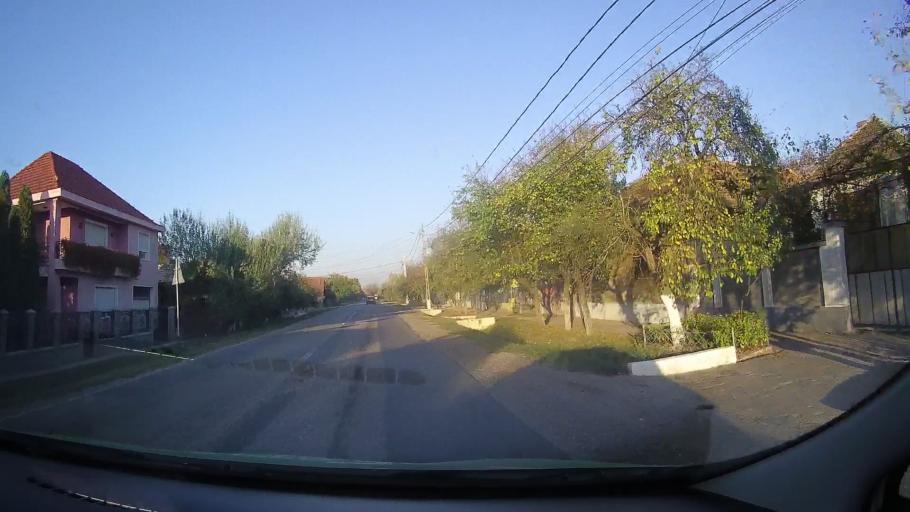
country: RO
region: Bihor
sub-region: Comuna Salard
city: Salard
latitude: 47.2187
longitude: 22.0348
